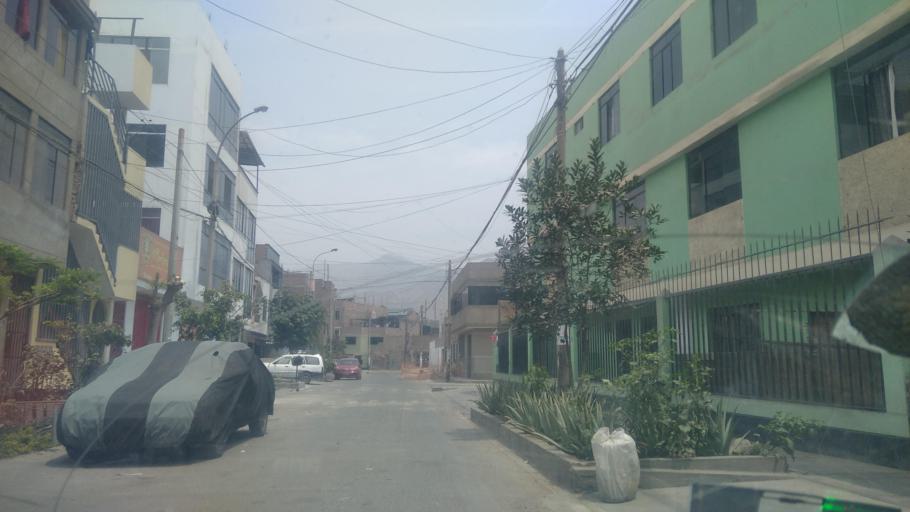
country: PE
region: Lima
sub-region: Lima
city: Independencia
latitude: -11.9856
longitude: -77.0090
